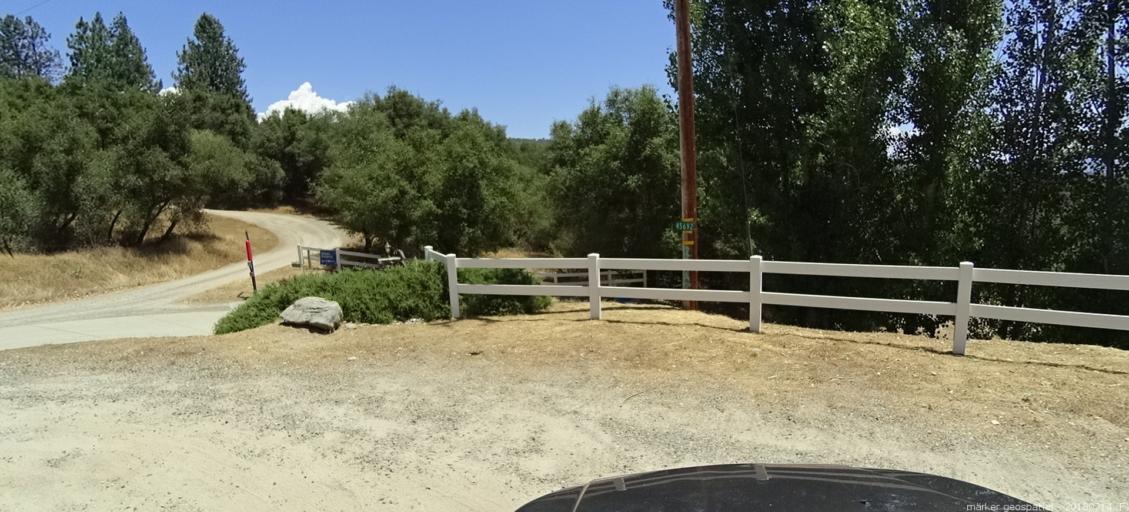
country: US
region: California
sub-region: Madera County
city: Ahwahnee
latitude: 37.3723
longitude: -119.7131
